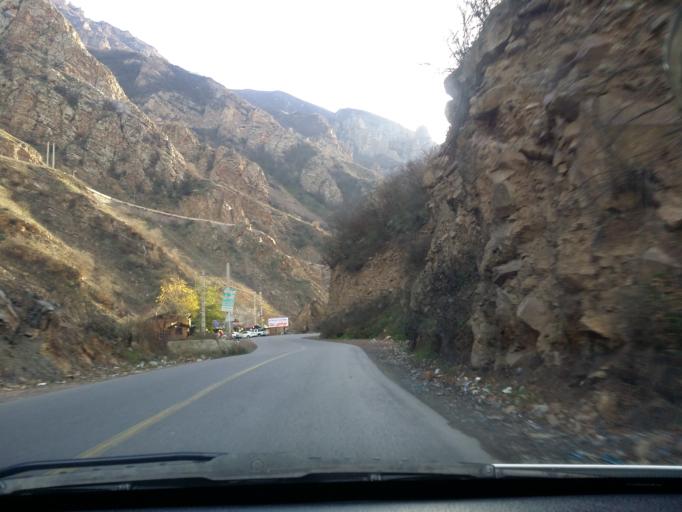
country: IR
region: Mazandaran
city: Chalus
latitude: 36.2649
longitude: 51.2590
